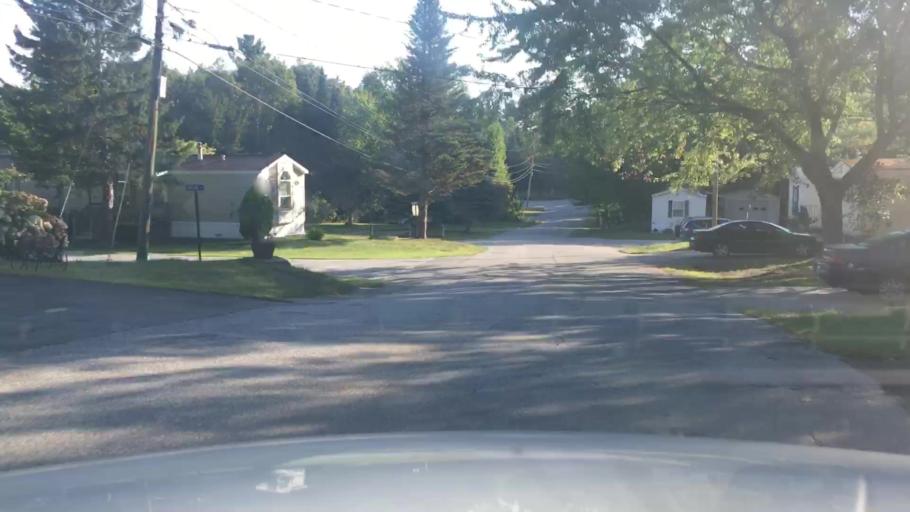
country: US
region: Maine
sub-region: Oxford County
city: Norway
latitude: 44.1994
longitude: -70.5365
